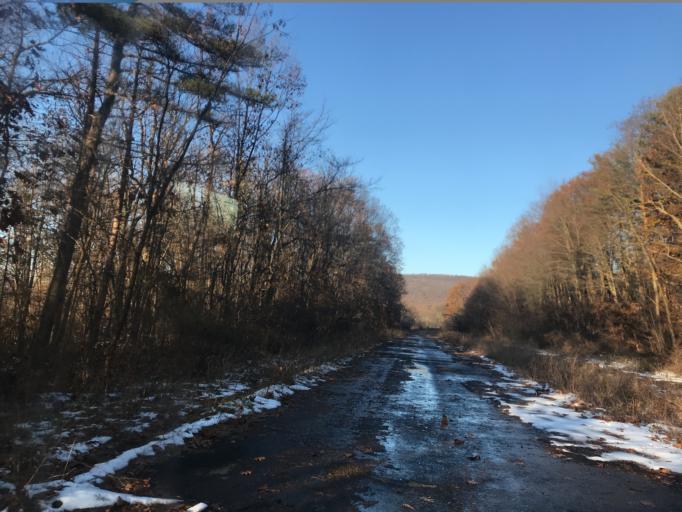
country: US
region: Pennsylvania
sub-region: Bedford County
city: Earlston
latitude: 40.0109
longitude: -78.2157
